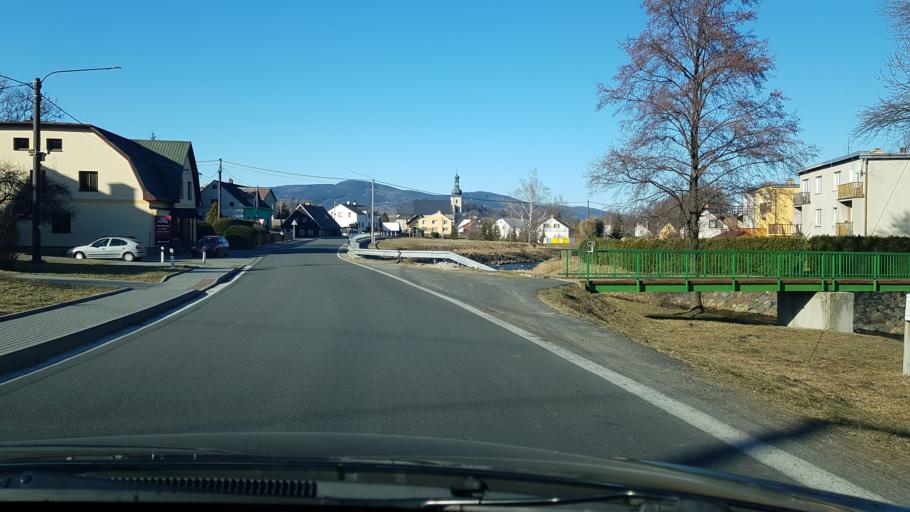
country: CZ
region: Olomoucky
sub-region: Okres Jesenik
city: Jesenik
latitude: 50.1879
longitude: 17.1953
